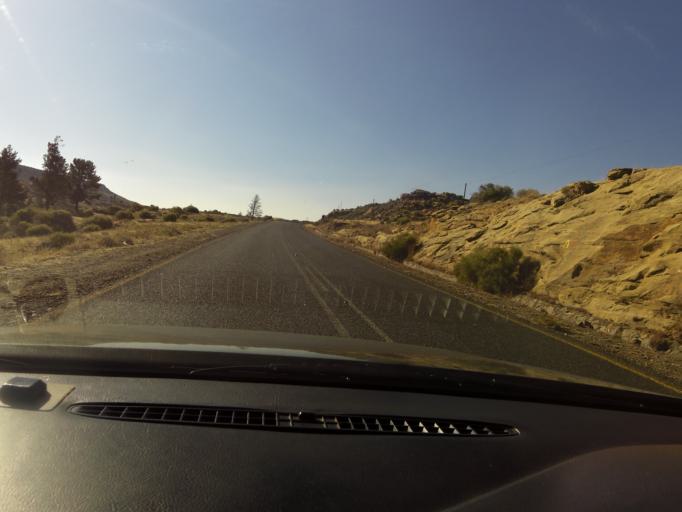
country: LS
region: Mohale's Hoek District
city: Mohale's Hoek
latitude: -30.0814
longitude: 27.4281
